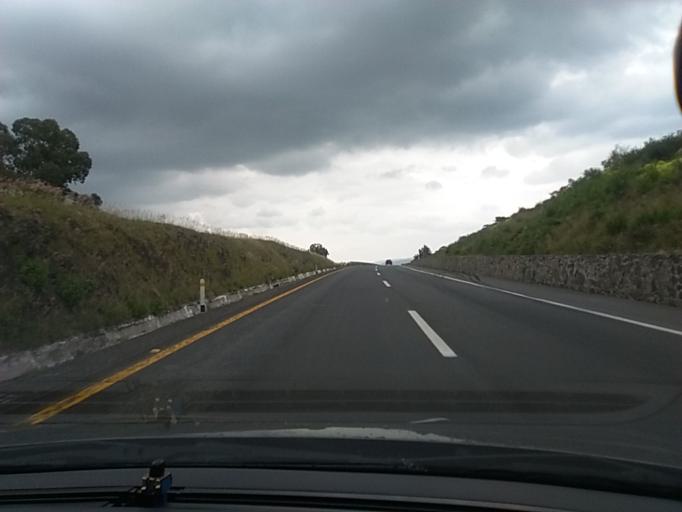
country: MX
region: Jalisco
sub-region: Poncitlan
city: Santa Cruz el Grande
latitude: 20.4432
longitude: -102.8341
